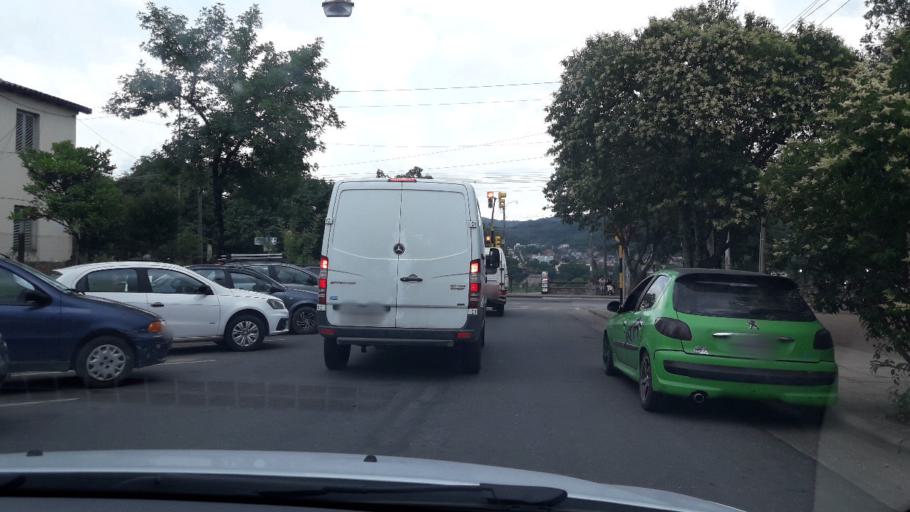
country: AR
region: Jujuy
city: San Salvador de Jujuy
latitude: -24.1804
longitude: -65.3129
